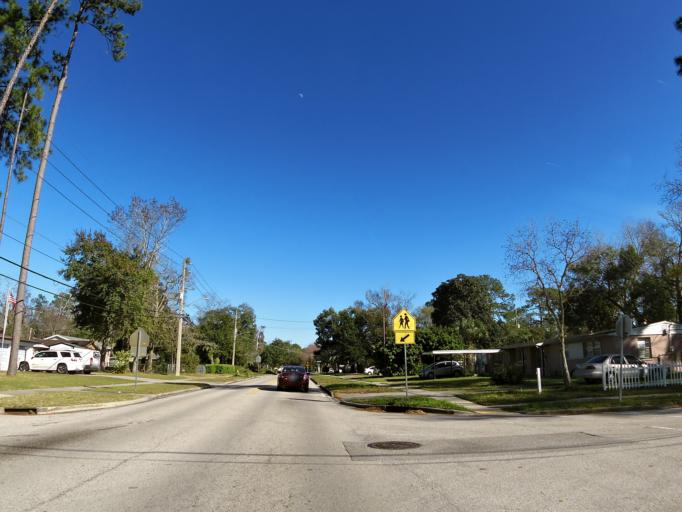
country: US
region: Florida
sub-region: Duval County
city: Jacksonville
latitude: 30.2820
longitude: -81.6166
